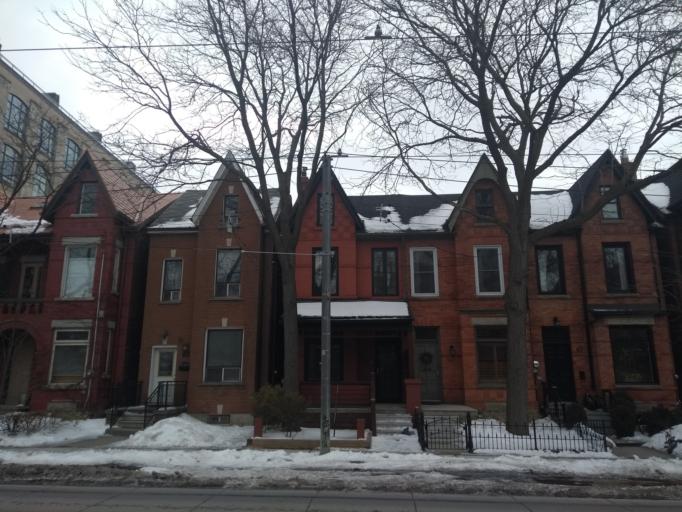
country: CA
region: Ontario
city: Toronto
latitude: 43.6441
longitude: -79.4161
